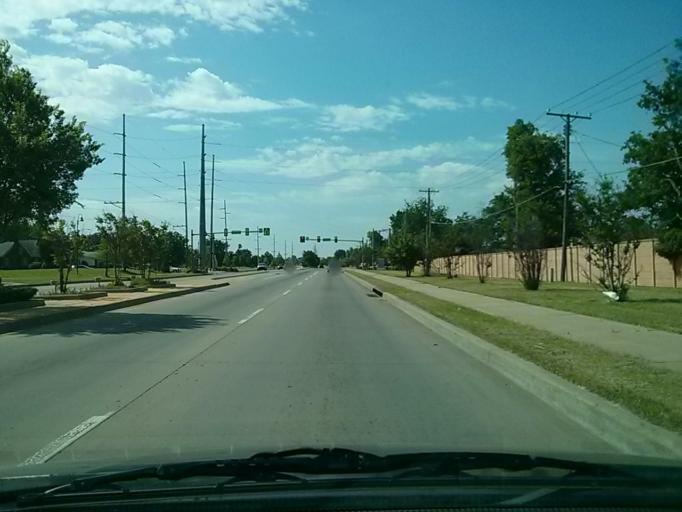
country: US
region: Oklahoma
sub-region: Tulsa County
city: Tulsa
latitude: 36.1853
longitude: -95.9760
